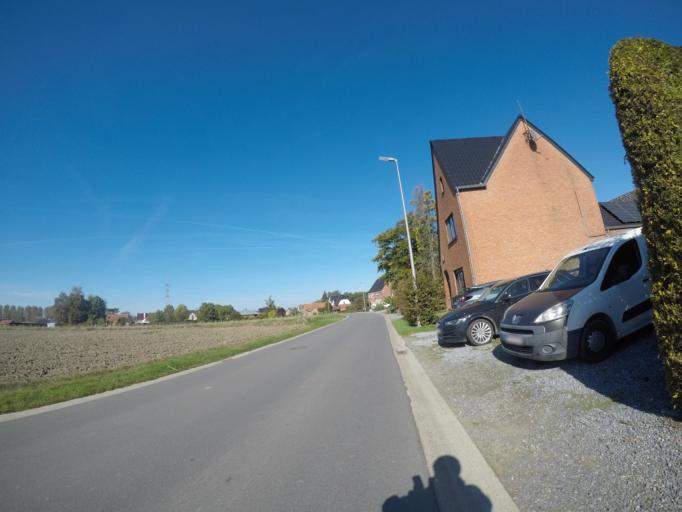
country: BE
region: Flanders
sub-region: Provincie Limburg
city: Alken
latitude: 50.8698
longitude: 5.2896
